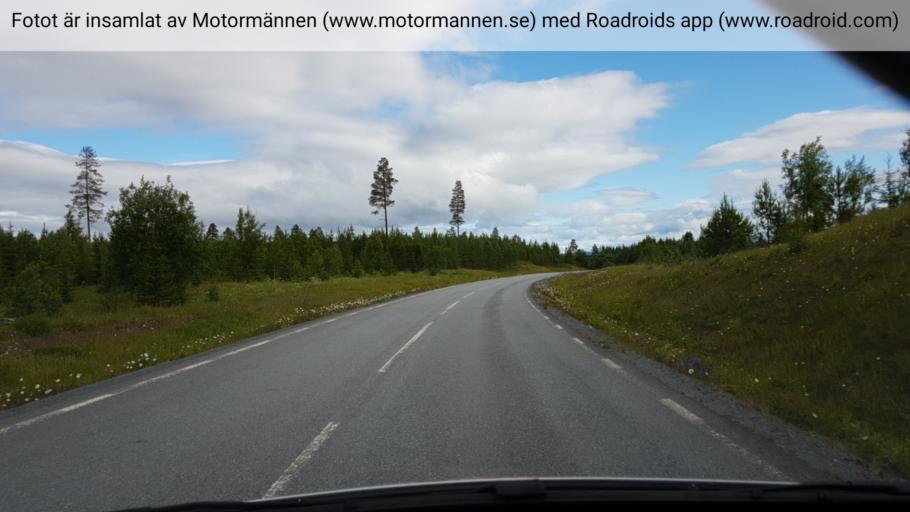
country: SE
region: Jaemtland
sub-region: Krokoms Kommun
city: Krokom
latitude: 63.2609
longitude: 14.4335
